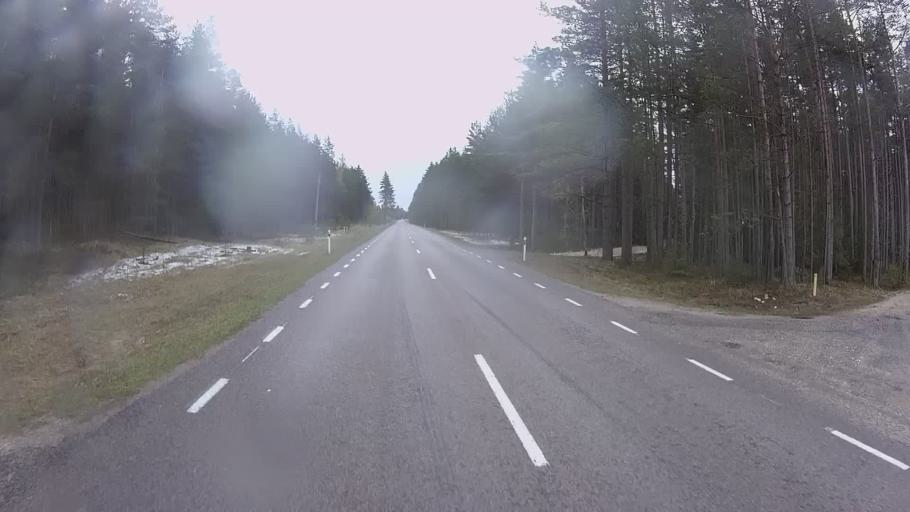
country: EE
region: Hiiumaa
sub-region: Kaerdla linn
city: Kardla
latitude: 58.9050
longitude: 22.4079
